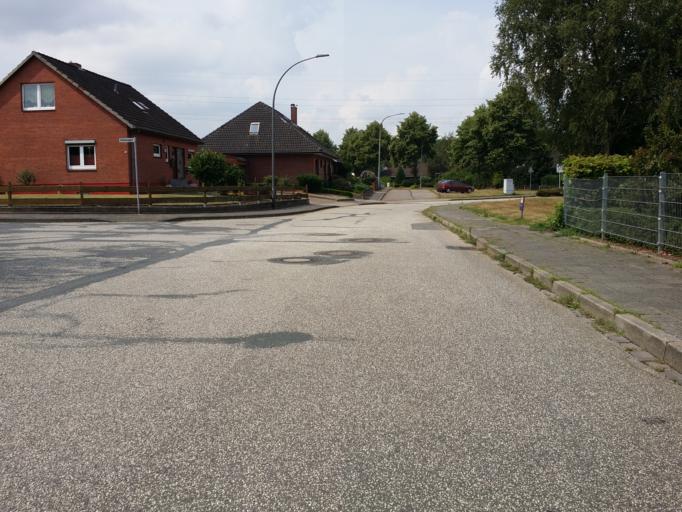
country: DE
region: Schleswig-Holstein
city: Heiligenstedtenerkamp
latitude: 53.9039
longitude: 9.4781
